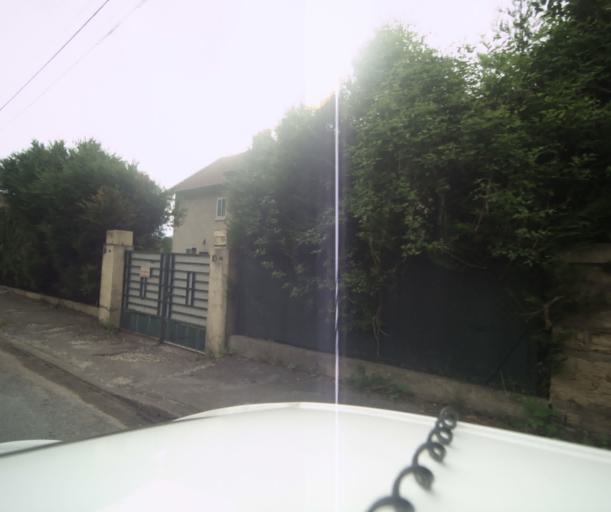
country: FR
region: Franche-Comte
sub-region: Departement du Doubs
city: Beure
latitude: 47.2130
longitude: 6.0024
